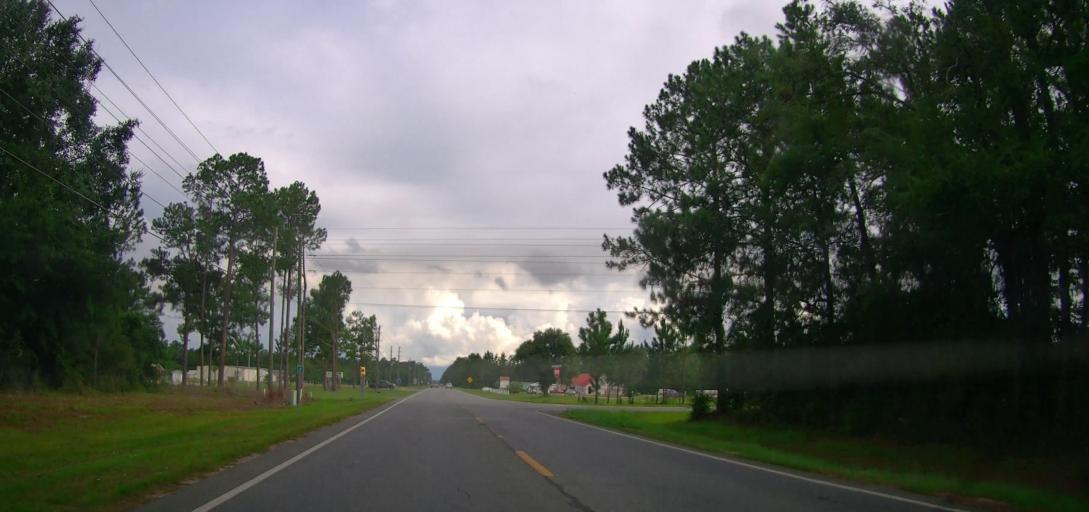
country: US
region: Georgia
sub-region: Wayne County
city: Jesup
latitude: 31.6450
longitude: -81.9074
